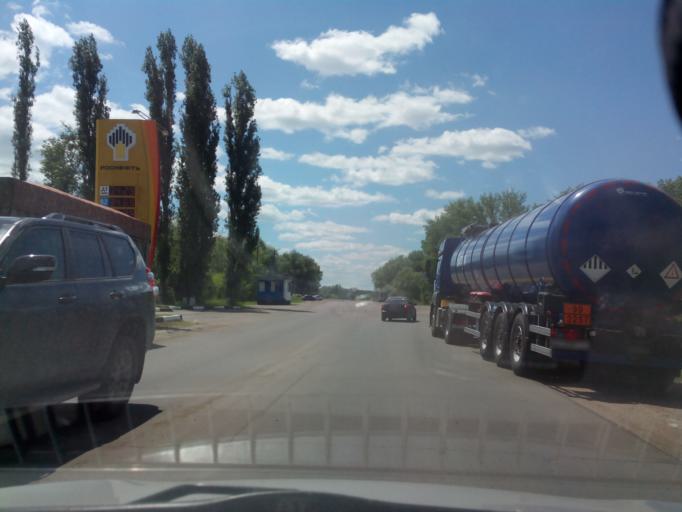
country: RU
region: Voronezj
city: Ternovka
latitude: 51.6719
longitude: 41.5817
